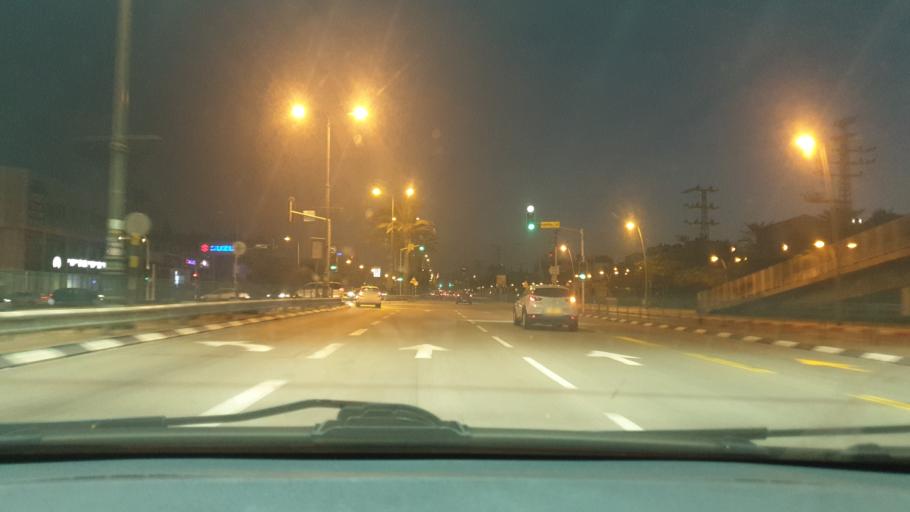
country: IL
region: Central District
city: Bet Dagan
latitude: 31.9841
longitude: 34.8104
